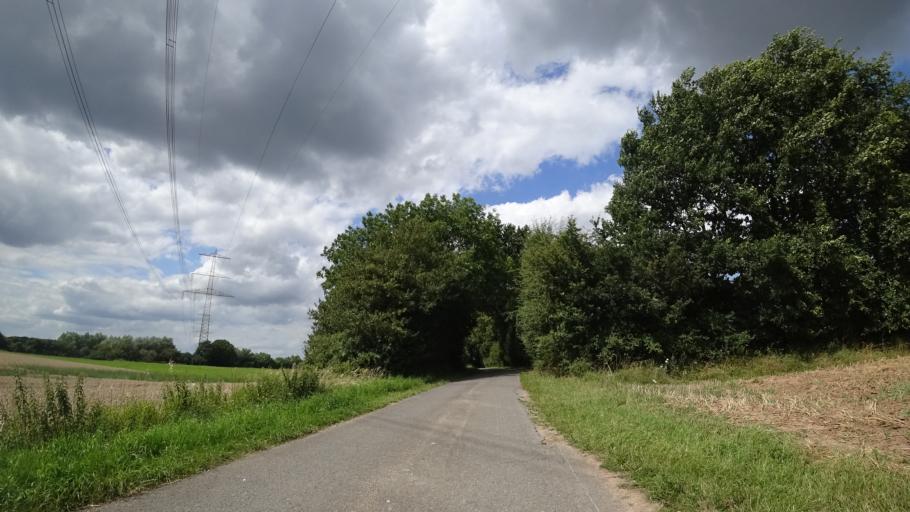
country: DE
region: North Rhine-Westphalia
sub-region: Regierungsbezirk Detmold
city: Petershagen
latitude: 52.3919
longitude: 8.9892
